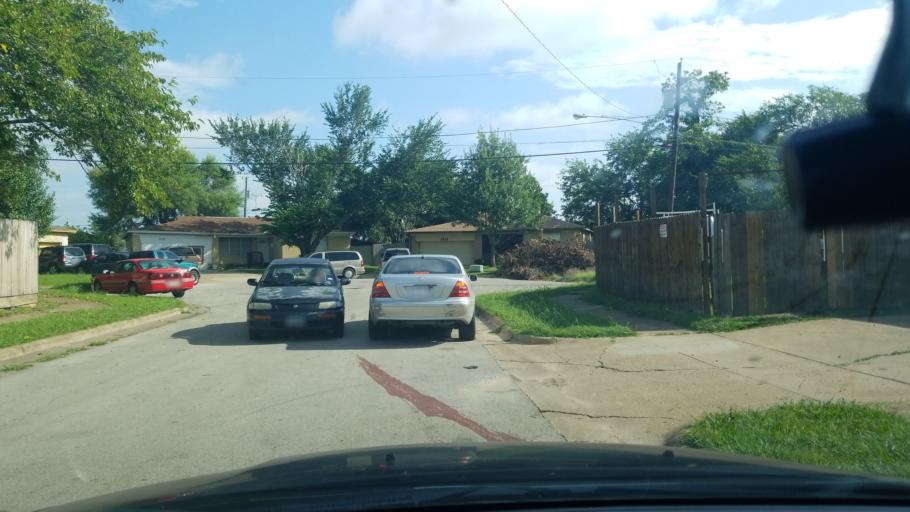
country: US
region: Texas
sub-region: Dallas County
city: Balch Springs
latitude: 32.7478
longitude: -96.6688
